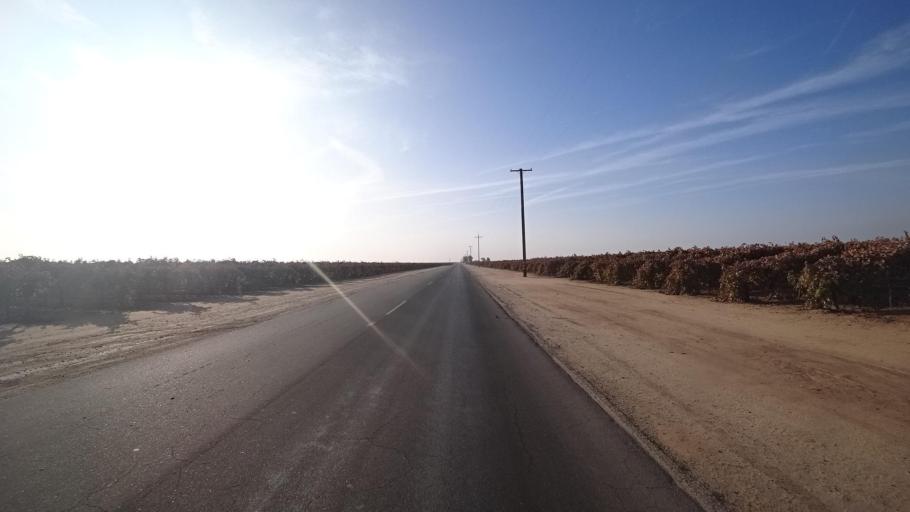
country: US
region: California
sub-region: Kern County
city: Delano
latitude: 35.7567
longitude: -119.1874
